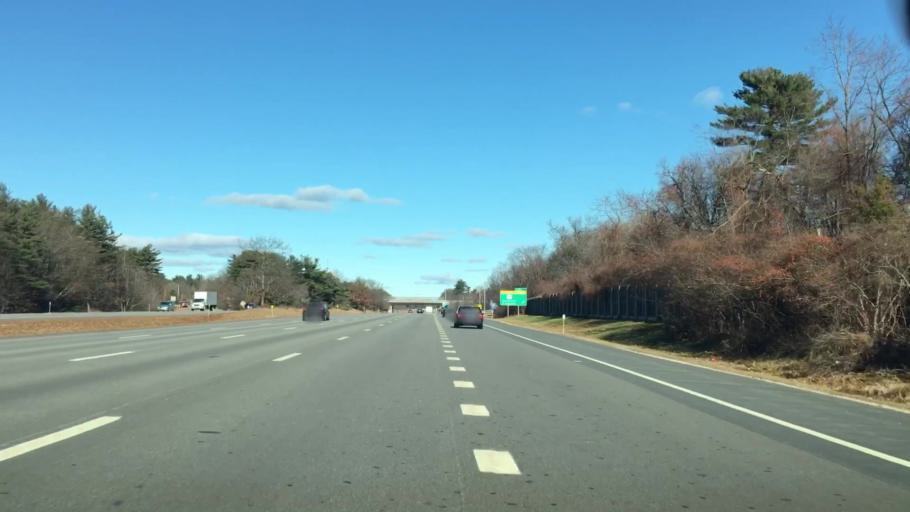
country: US
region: New Hampshire
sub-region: Rockingham County
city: Seabrook
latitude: 42.8898
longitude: -70.8807
